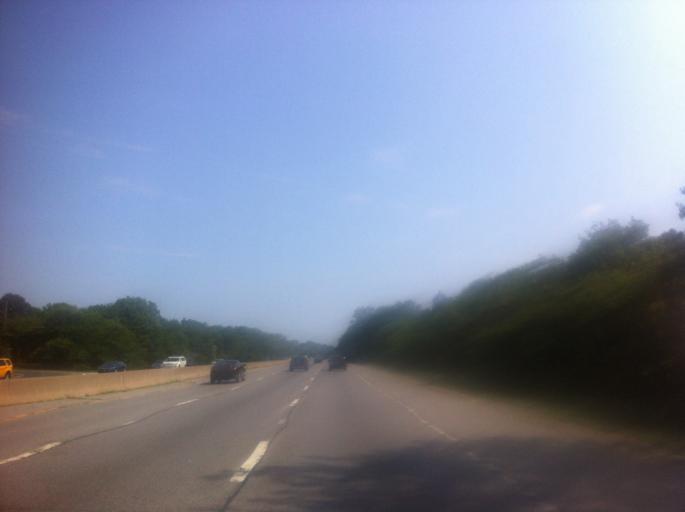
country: US
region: New York
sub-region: Nassau County
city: Plainview
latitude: 40.7936
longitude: -73.4875
